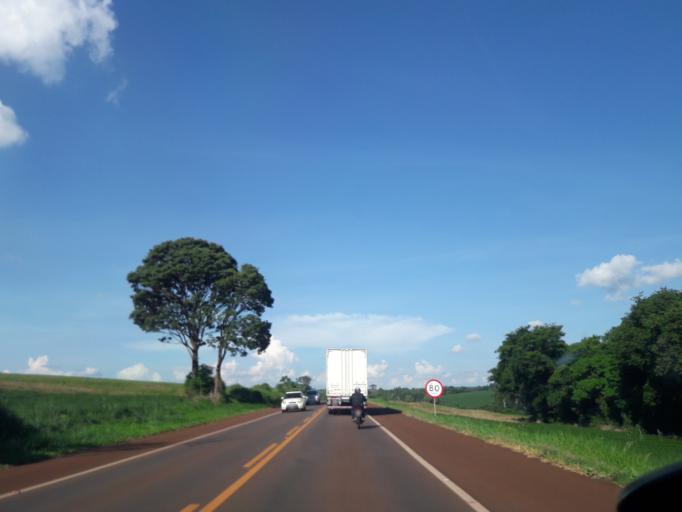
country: BR
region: Parana
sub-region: Campo Mourao
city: Campo Mourao
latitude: -24.3256
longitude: -52.6497
